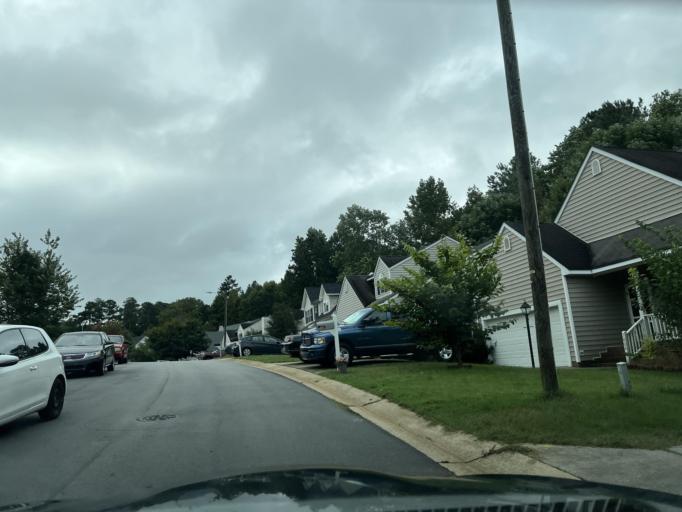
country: US
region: North Carolina
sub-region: Wake County
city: West Raleigh
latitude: 35.7492
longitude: -78.6817
